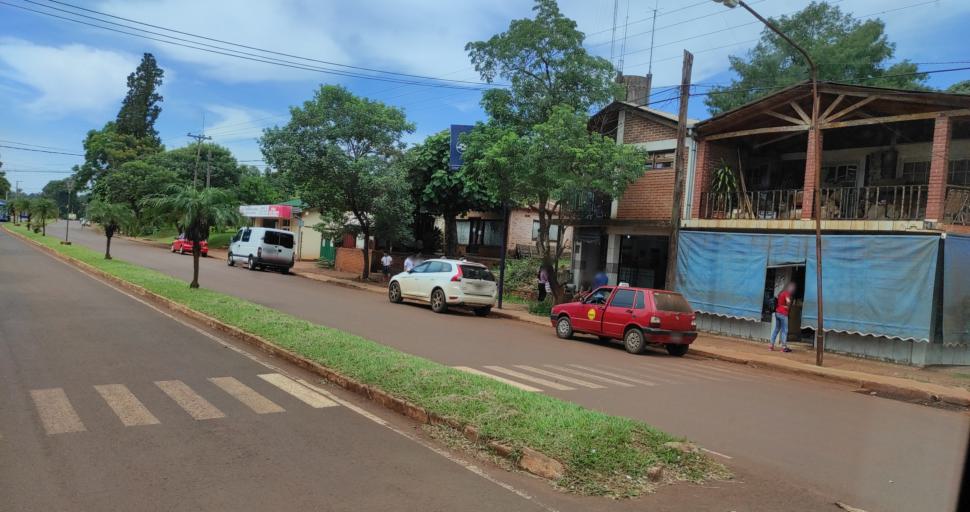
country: AR
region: Misiones
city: El Alcazar
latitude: -26.7146
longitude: -54.8144
